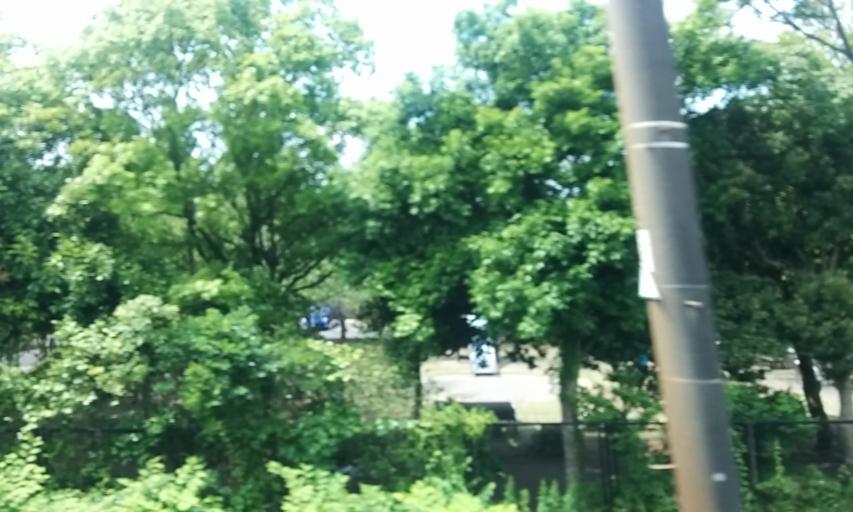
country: JP
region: Chiba
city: Sakura
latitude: 35.7284
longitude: 140.2185
